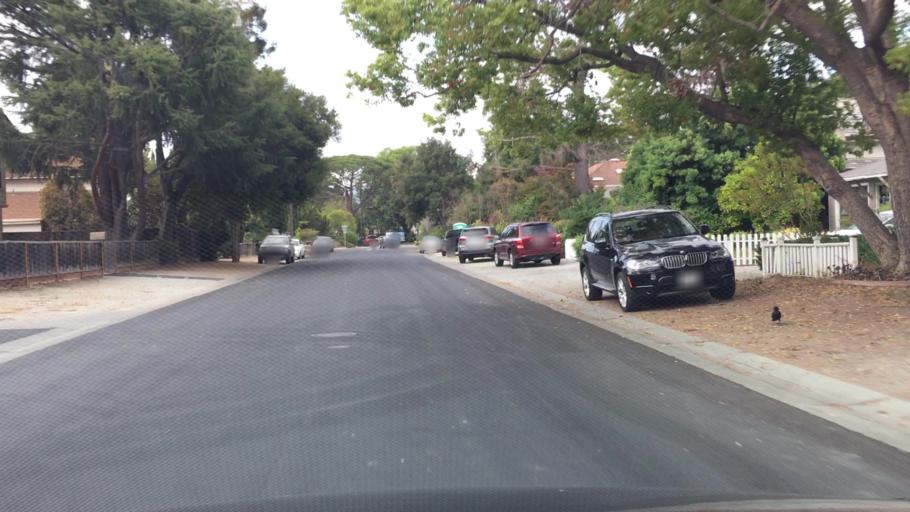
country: US
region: California
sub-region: Santa Clara County
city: Los Altos
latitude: 37.4095
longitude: -122.1285
